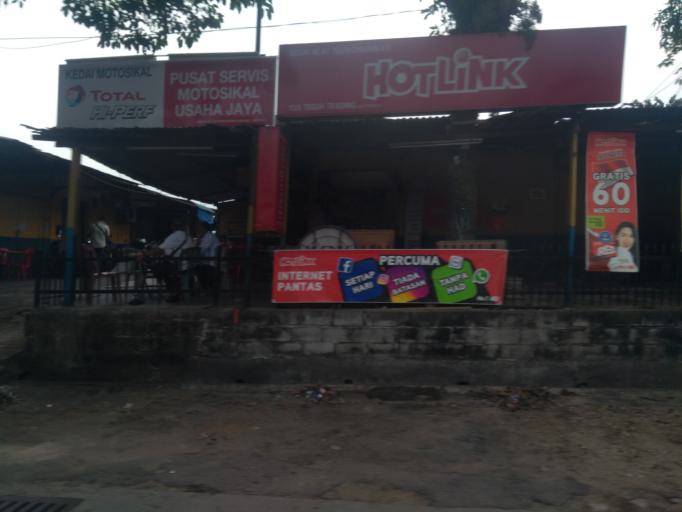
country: MY
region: Johor
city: Johor Bahru
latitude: 1.4916
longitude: 103.7084
